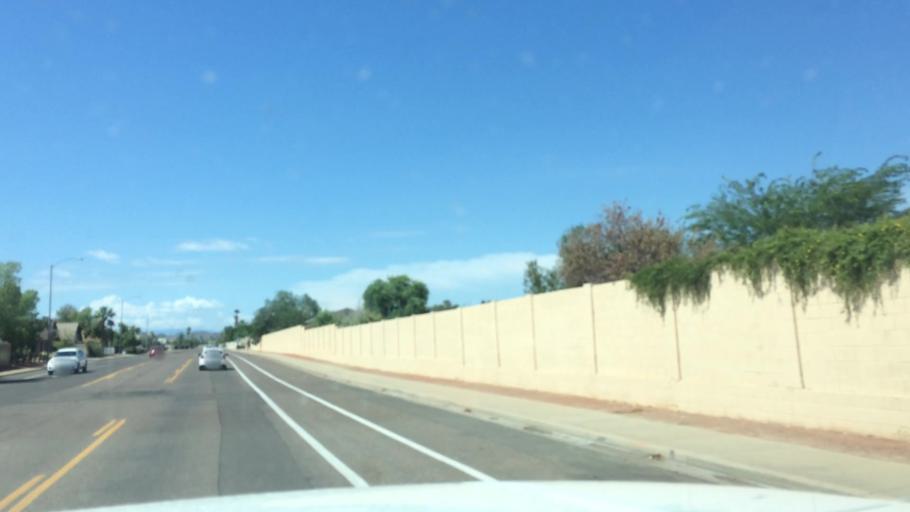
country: US
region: Arizona
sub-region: Maricopa County
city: Sun City
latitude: 33.6429
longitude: -112.2463
